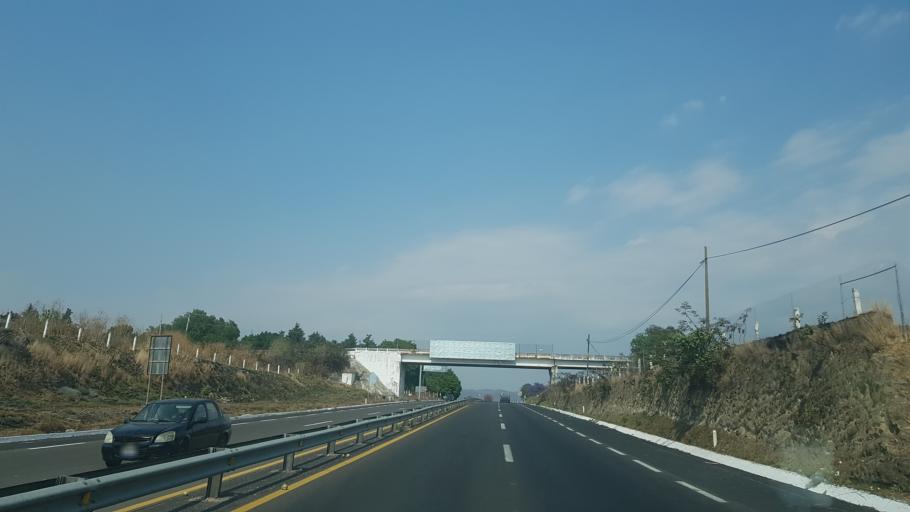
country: MX
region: Puebla
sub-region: Atlixco
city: San Agustin Huixaxtla
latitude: 18.9227
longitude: -98.4047
